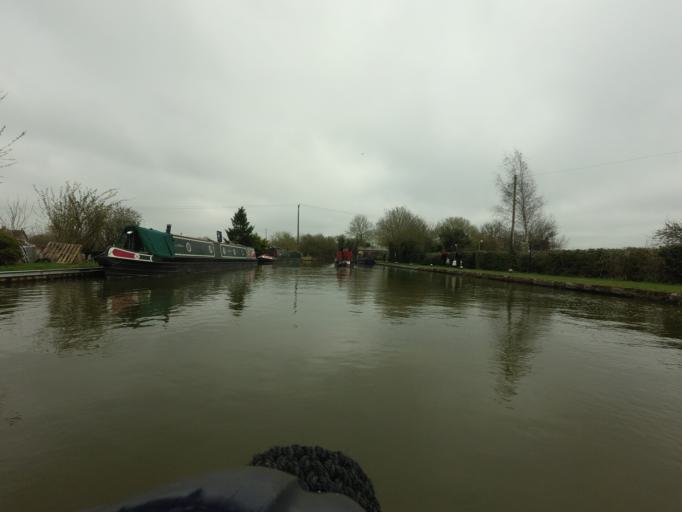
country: GB
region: England
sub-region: Buckinghamshire
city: Cheddington
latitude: 51.8732
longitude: -0.6519
